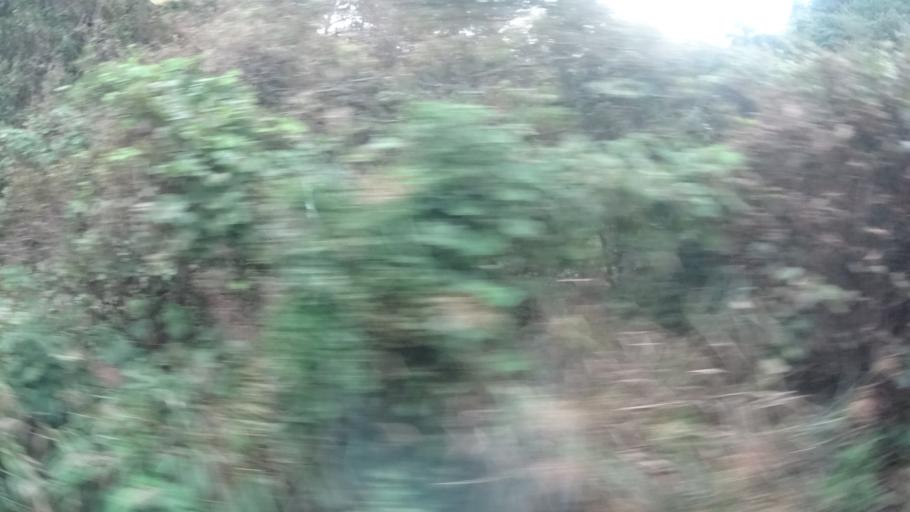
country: JP
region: Niigata
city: Murakami
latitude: 38.3828
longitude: 139.4605
